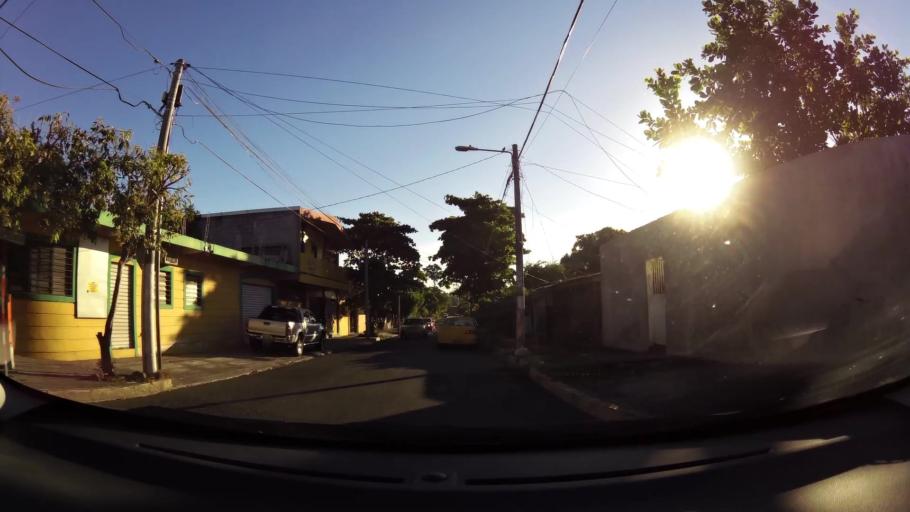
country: SV
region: San Miguel
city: San Miguel
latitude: 13.4873
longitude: -88.1712
